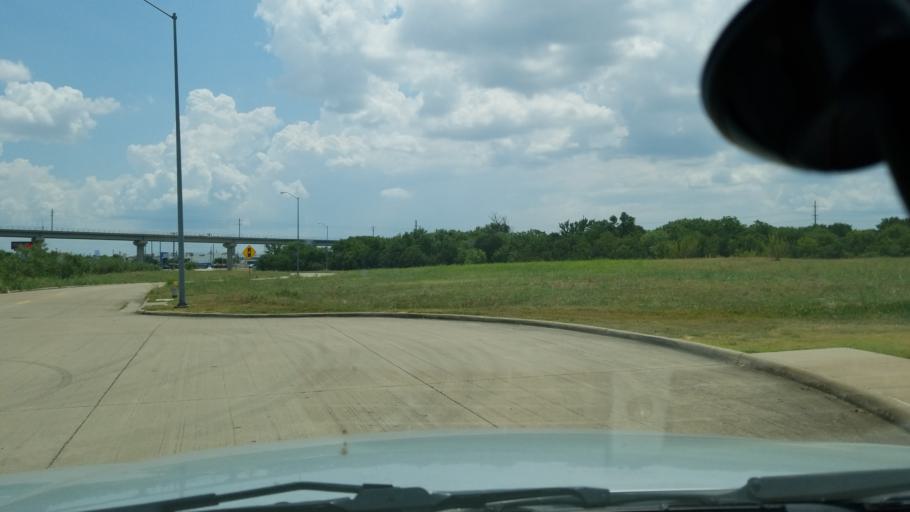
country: US
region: Texas
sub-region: Dallas County
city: Farmers Branch
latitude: 32.8552
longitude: -96.8885
